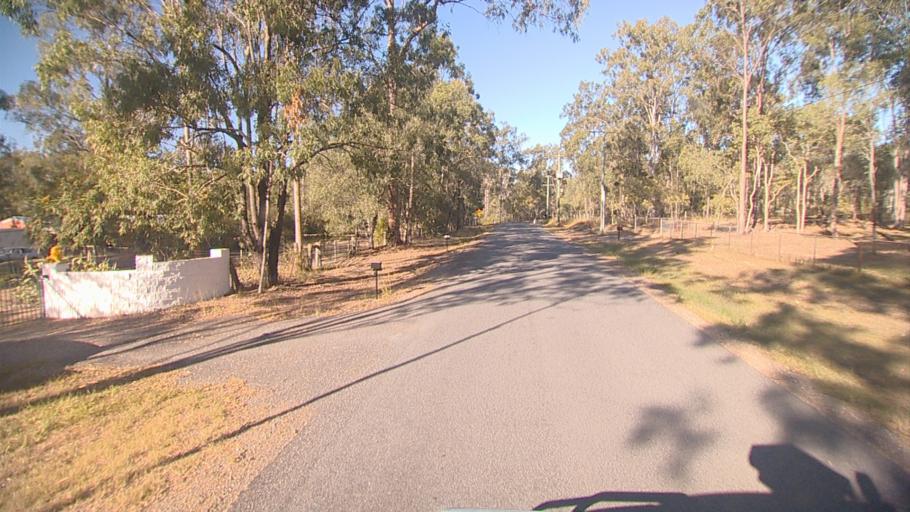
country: AU
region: Queensland
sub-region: Logan
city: North Maclean
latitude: -27.7840
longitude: 152.9854
